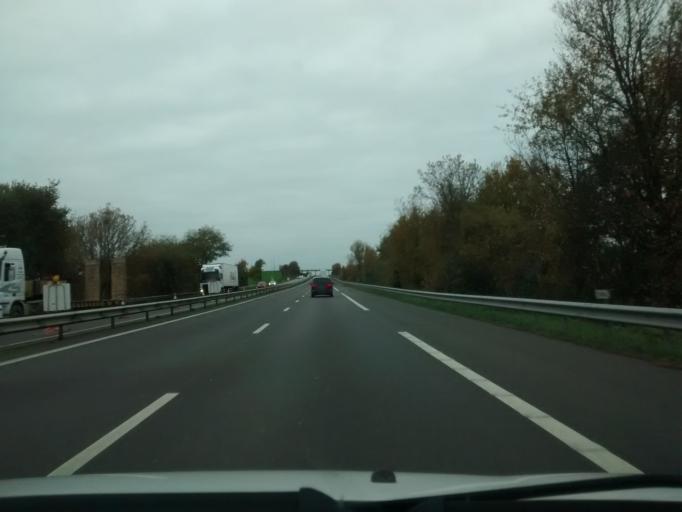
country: FR
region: Brittany
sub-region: Departement d'Ille-et-Vilaine
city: Saint-Didier
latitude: 48.0890
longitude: -1.3670
